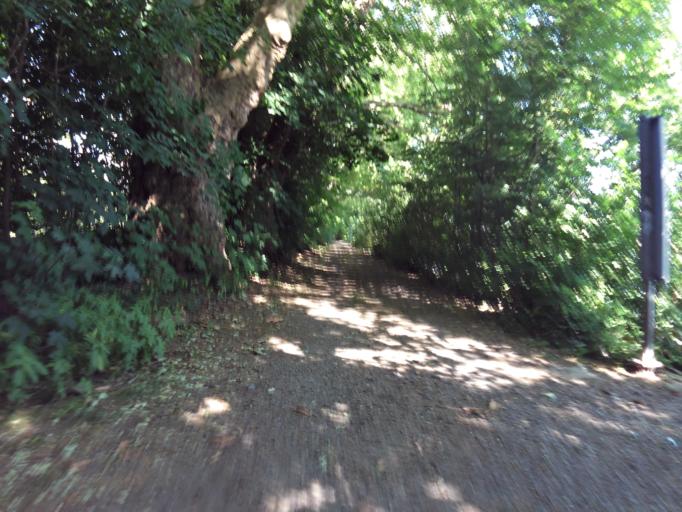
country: DE
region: Rheinland-Pfalz
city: Worms
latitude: 49.6114
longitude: 8.3959
